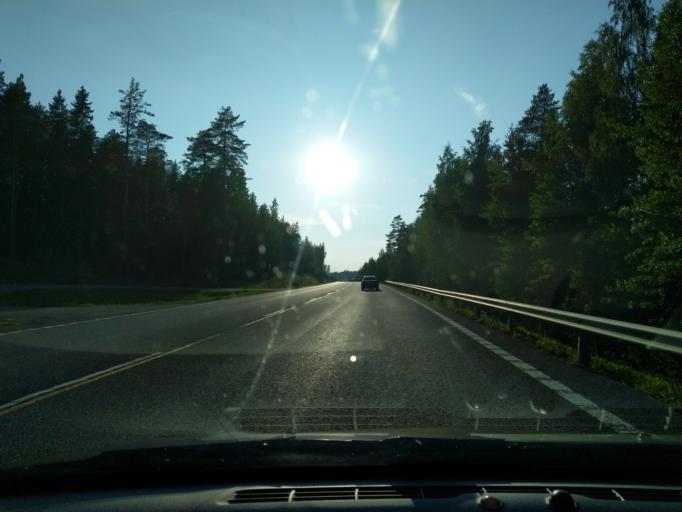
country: FI
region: Paijanne Tavastia
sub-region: Lahti
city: Lahti
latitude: 60.9663
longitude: 25.7398
